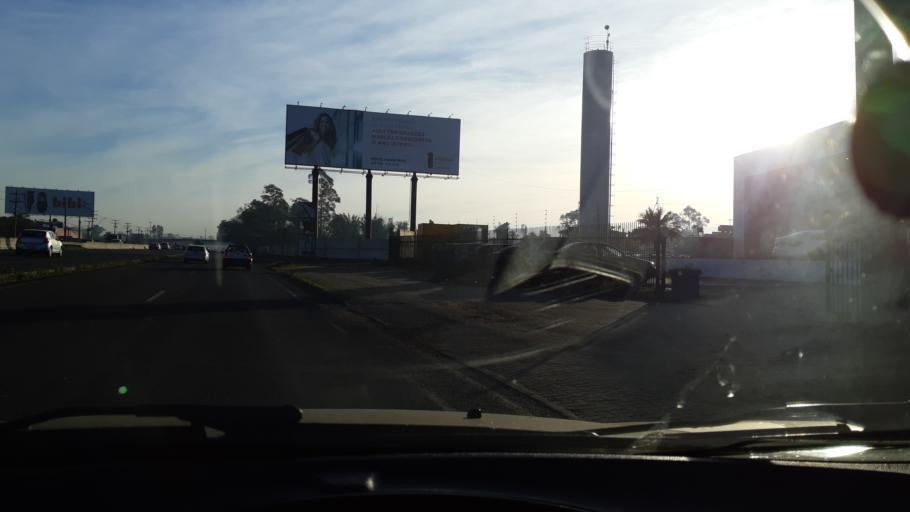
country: BR
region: Rio Grande do Sul
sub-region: Sapucaia Do Sul
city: Sapucaia
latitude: -29.8342
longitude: -51.1744
